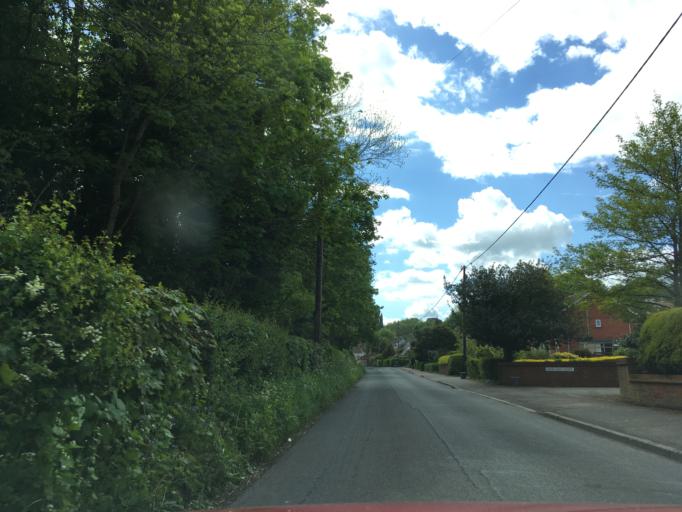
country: GB
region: England
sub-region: Gloucestershire
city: Dursley
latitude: 51.6933
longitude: -2.3561
